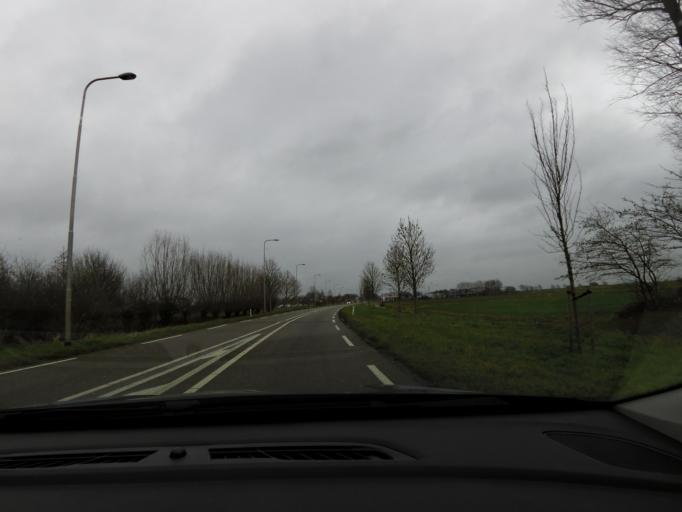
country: NL
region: North Brabant
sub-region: Gemeente Woudrichem
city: Almkerk
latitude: 51.7304
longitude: 4.9512
